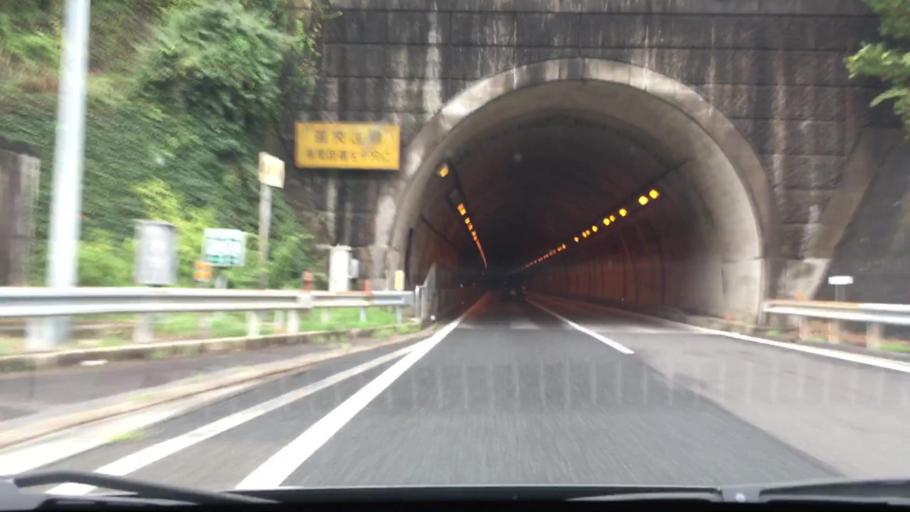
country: JP
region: Hiroshima
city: Hiroshima-shi
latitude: 34.5136
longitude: 132.4200
